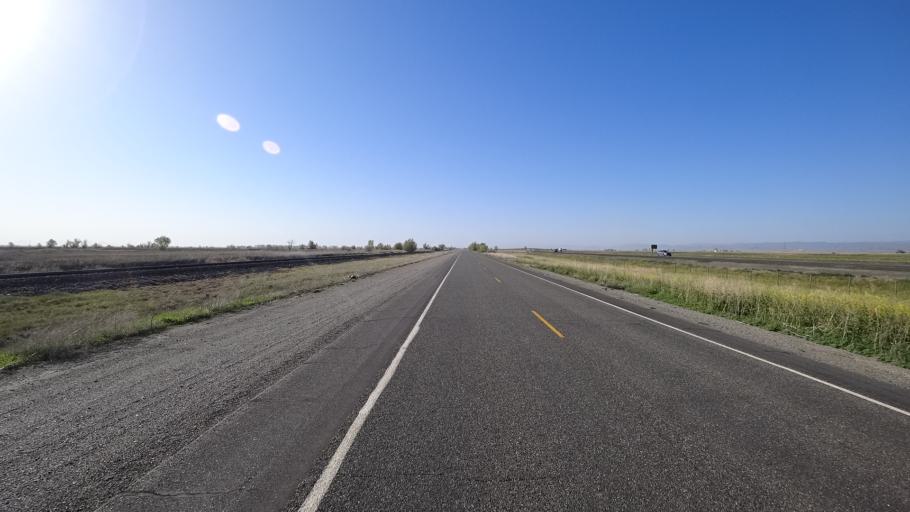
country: US
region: California
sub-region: Glenn County
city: Willows
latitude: 39.4210
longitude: -122.1926
